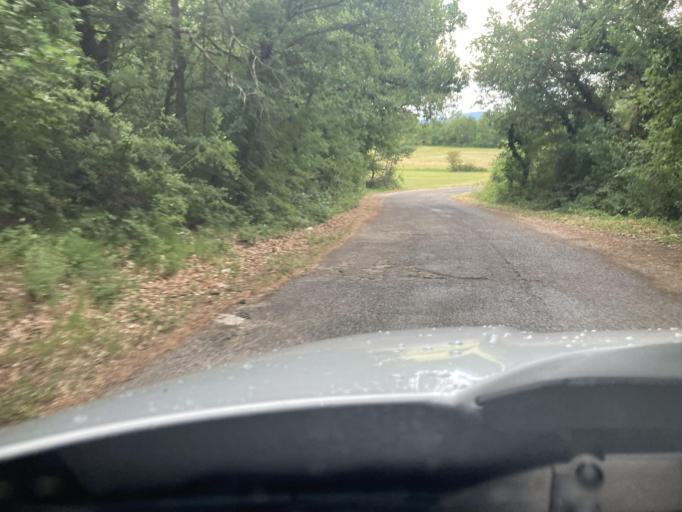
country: IT
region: Abruzzo
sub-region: Provincia dell' Aquila
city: San Panfilo d'Ocre
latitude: 42.2844
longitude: 13.4786
